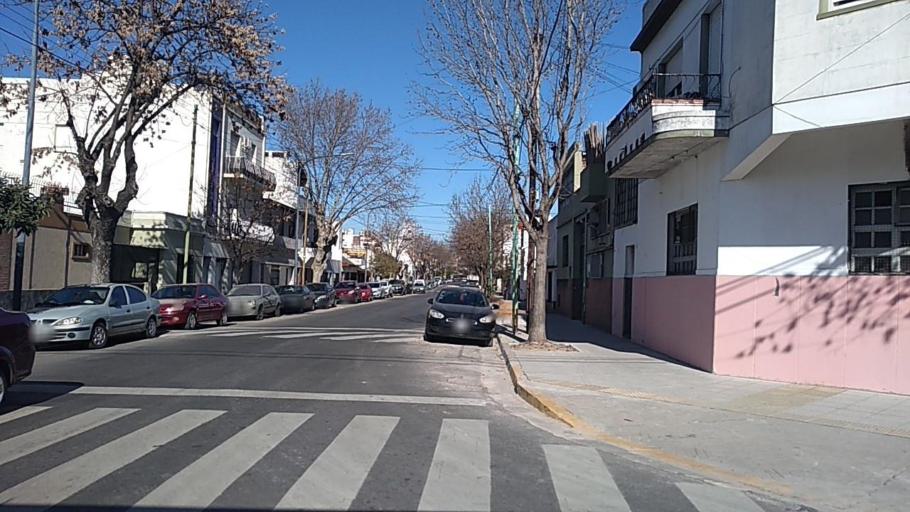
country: AR
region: Buenos Aires F.D.
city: Villa Santa Rita
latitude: -34.6191
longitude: -58.4955
